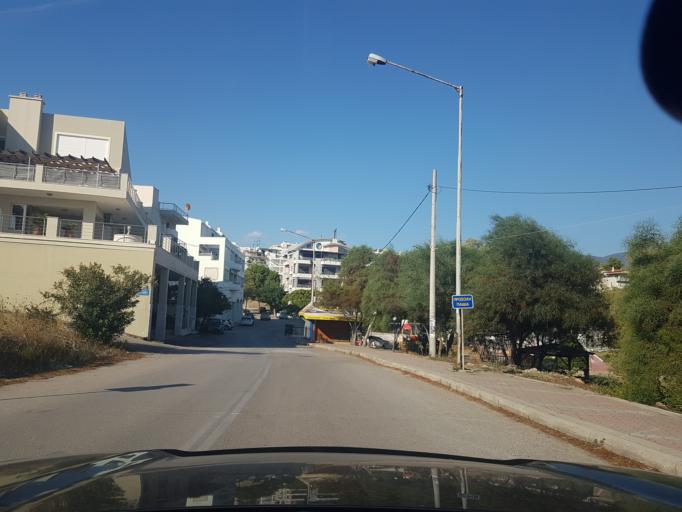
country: GR
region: Central Greece
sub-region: Nomos Evvoias
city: Chalkida
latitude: 38.4758
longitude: 23.5887
